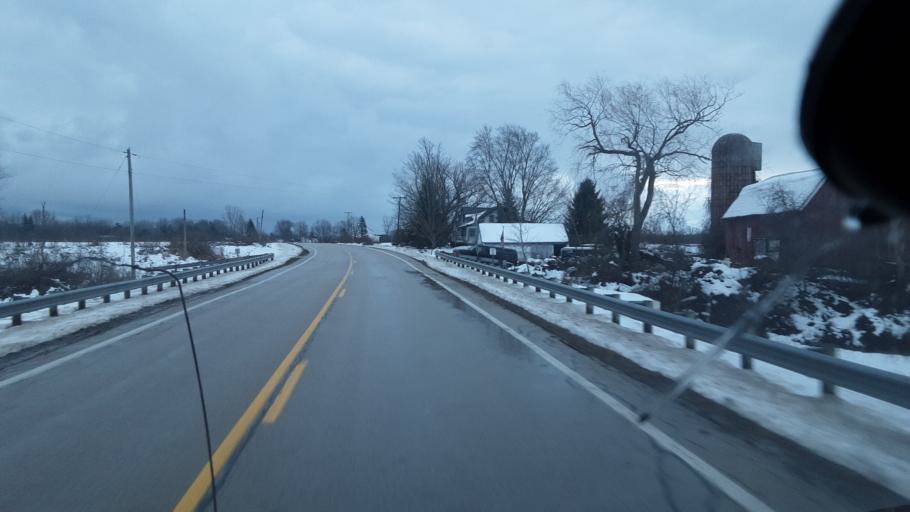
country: US
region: Ohio
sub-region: Ashtabula County
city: Jefferson
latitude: 41.6991
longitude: -80.7043
